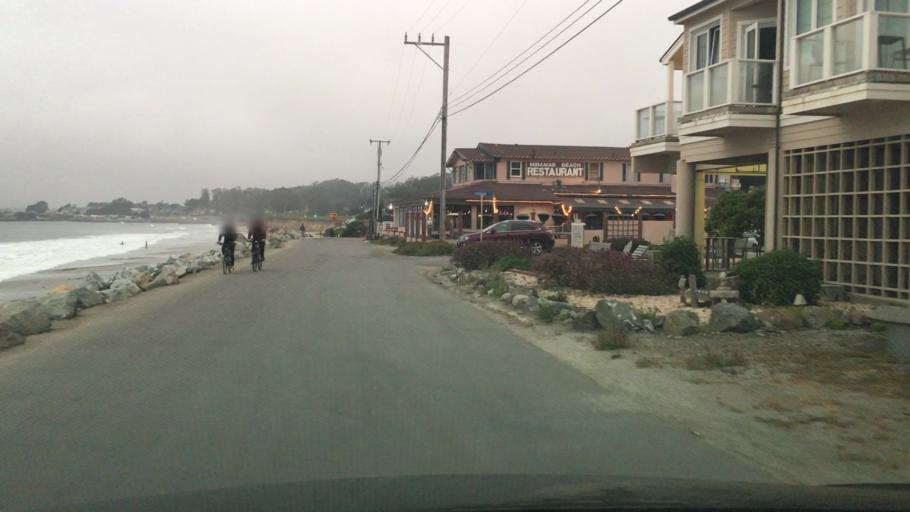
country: US
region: California
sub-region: San Mateo County
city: El Granada
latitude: 37.4950
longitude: -122.4620
